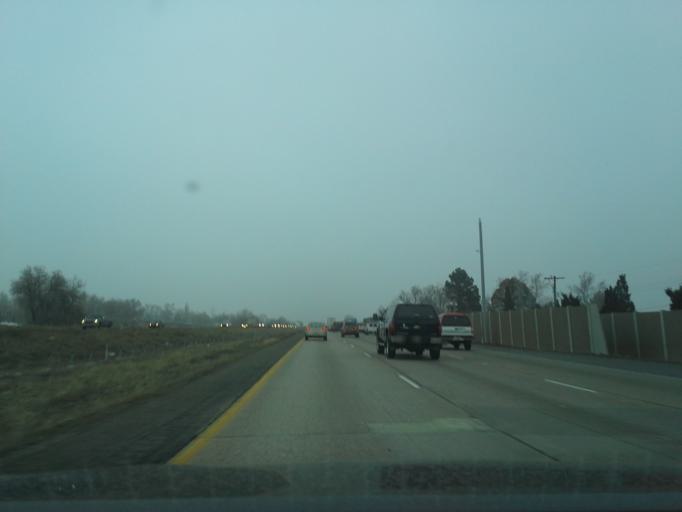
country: US
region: Utah
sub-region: Davis County
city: Clearfield
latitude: 41.1142
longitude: -112.0139
